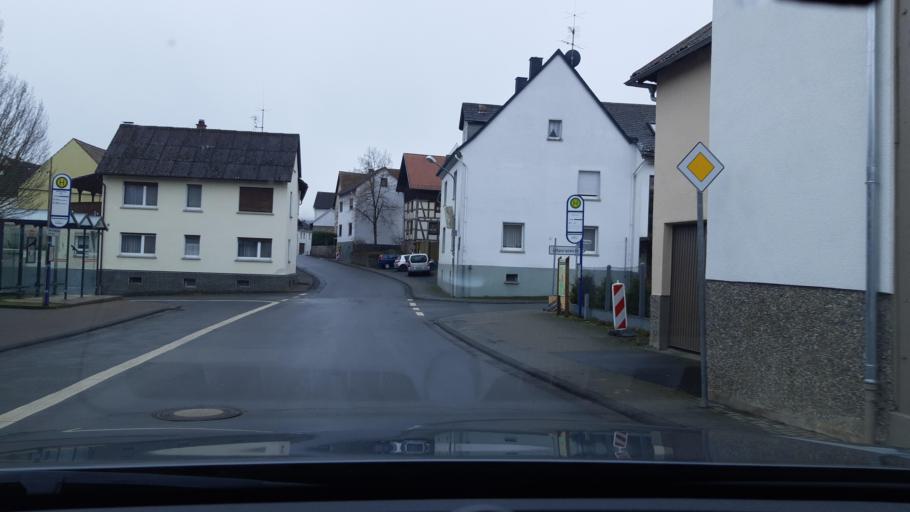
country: DE
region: Hesse
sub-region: Regierungsbezirk Giessen
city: Schoeffengrund
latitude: 50.4918
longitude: 8.5513
